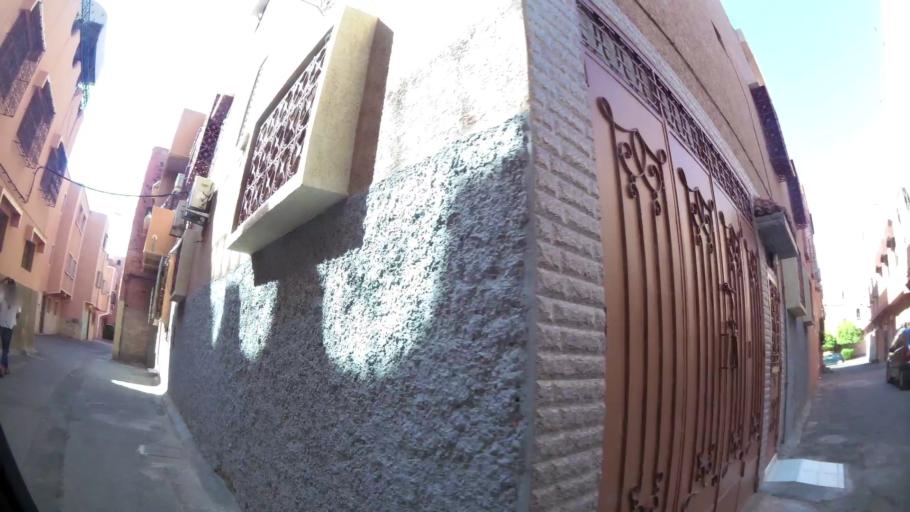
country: MA
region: Marrakech-Tensift-Al Haouz
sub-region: Marrakech
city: Marrakesh
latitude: 31.6553
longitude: -8.0169
